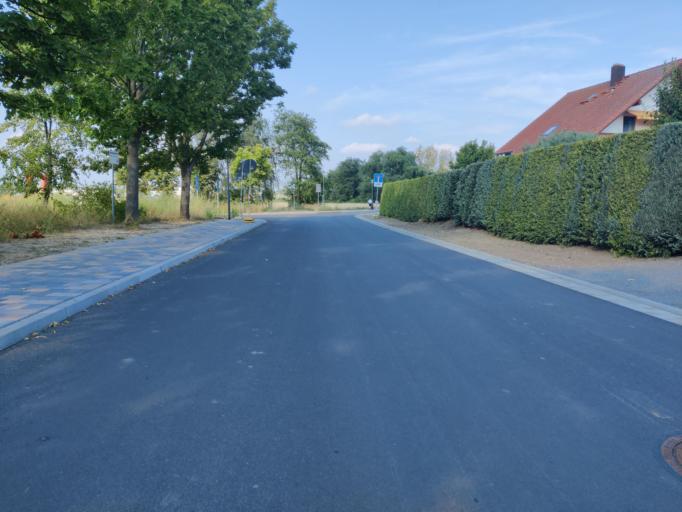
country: DE
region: Saxony
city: Neukieritzsch
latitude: 51.1678
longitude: 12.4357
